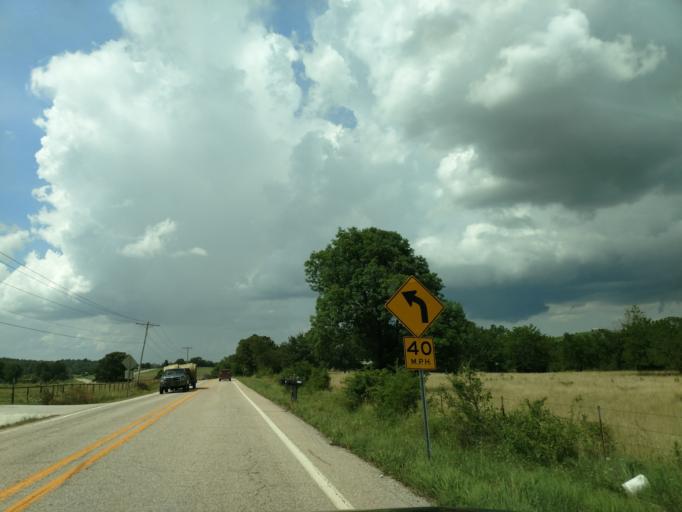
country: US
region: Arkansas
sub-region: Boone County
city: Harrison
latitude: 36.2687
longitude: -93.2321
